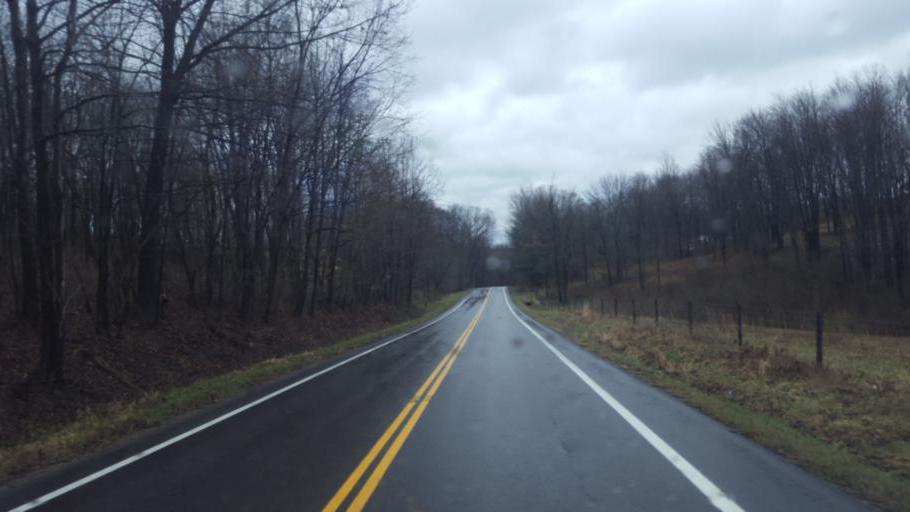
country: US
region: Ohio
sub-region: Sandusky County
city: Bellville
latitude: 40.6224
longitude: -82.3979
